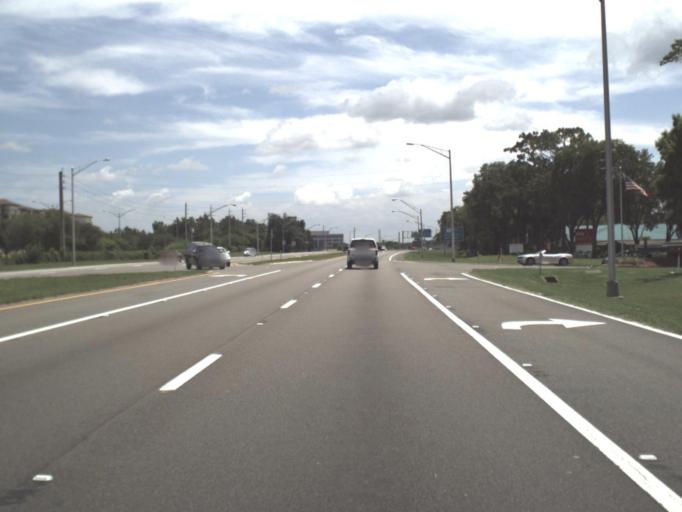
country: US
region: Florida
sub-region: Duval County
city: Jacksonville
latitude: 30.2574
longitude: -81.5551
